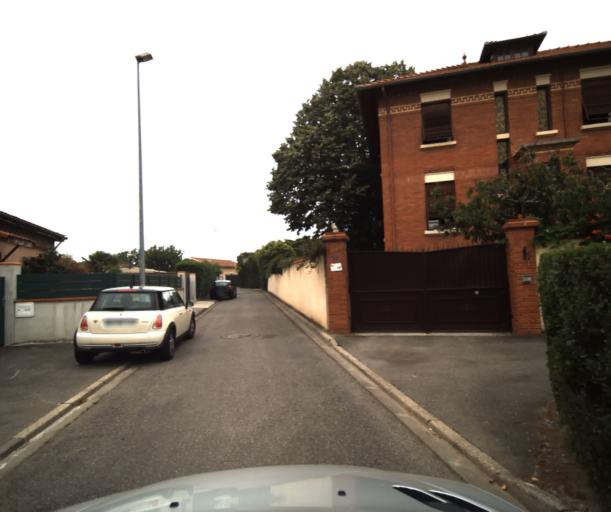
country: FR
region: Midi-Pyrenees
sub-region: Departement de la Haute-Garonne
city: Portet-sur-Garonne
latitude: 43.5232
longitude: 1.3984
